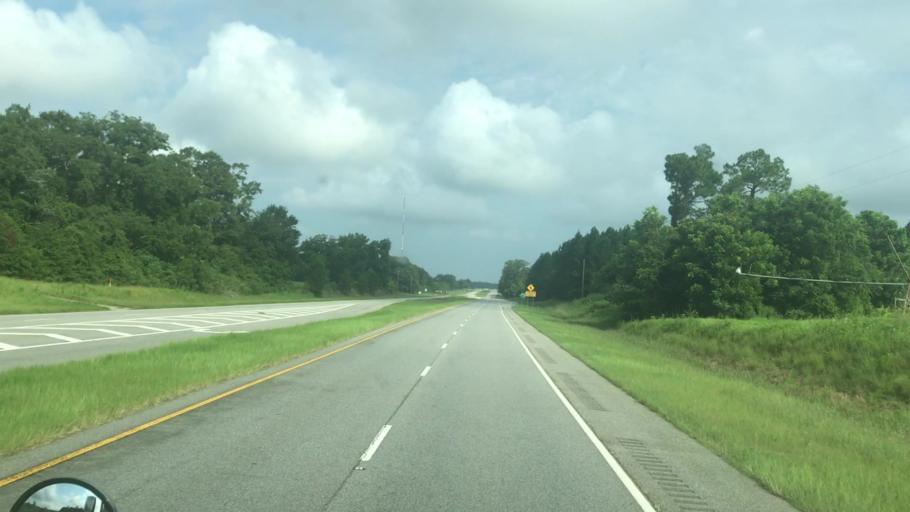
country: US
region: Georgia
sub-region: Miller County
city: Colquitt
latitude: 31.2570
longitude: -84.8075
